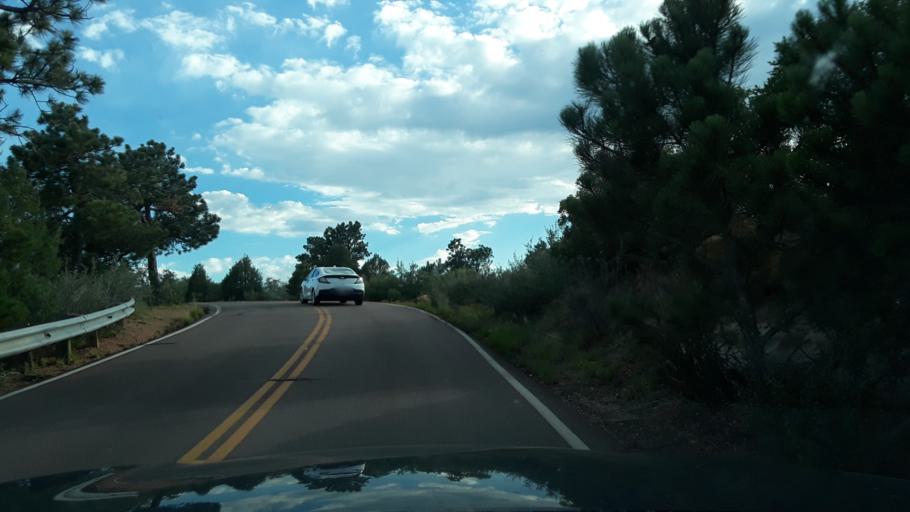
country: US
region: Colorado
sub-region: El Paso County
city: Colorado Springs
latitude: 38.8724
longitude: -104.7697
